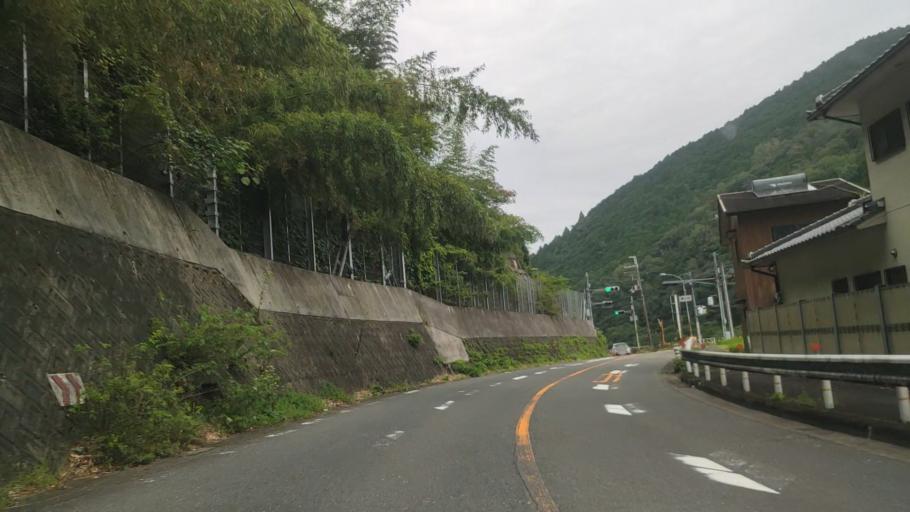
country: JP
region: Wakayama
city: Hashimoto
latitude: 34.3911
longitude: 135.5983
